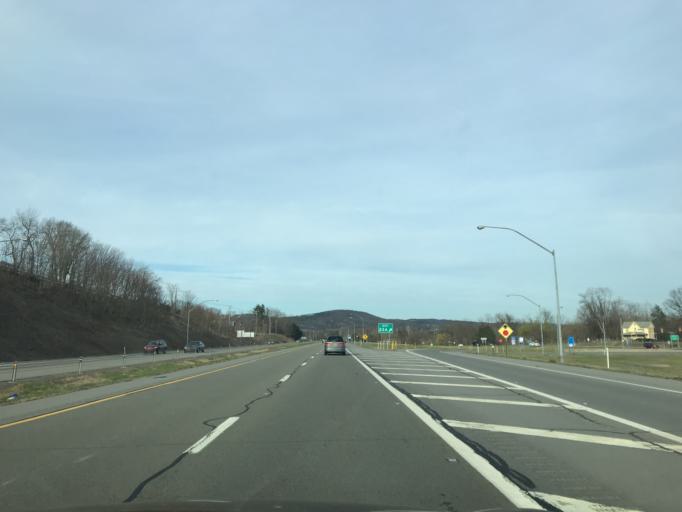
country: US
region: Pennsylvania
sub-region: Lycoming County
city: Kenmar
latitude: 41.2476
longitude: -76.9435
